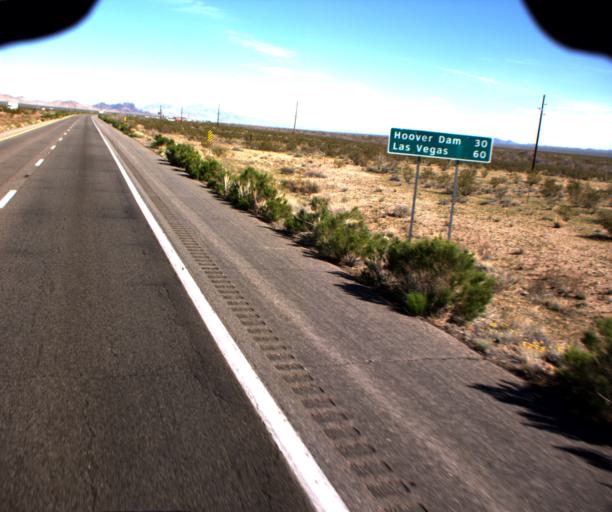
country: US
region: Arizona
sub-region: Mohave County
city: Dolan Springs
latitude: 35.6759
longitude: -114.4630
